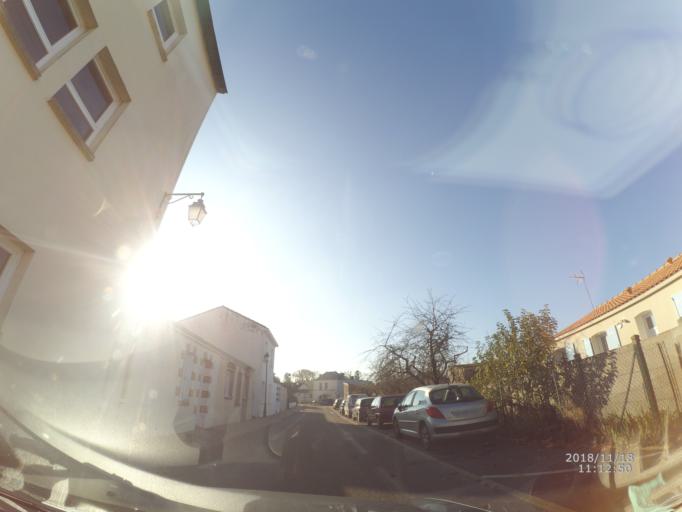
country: FR
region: Pays de la Loire
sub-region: Departement de la Loire-Atlantique
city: Saint-Pere-en-Retz
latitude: 47.2050
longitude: -2.0429
